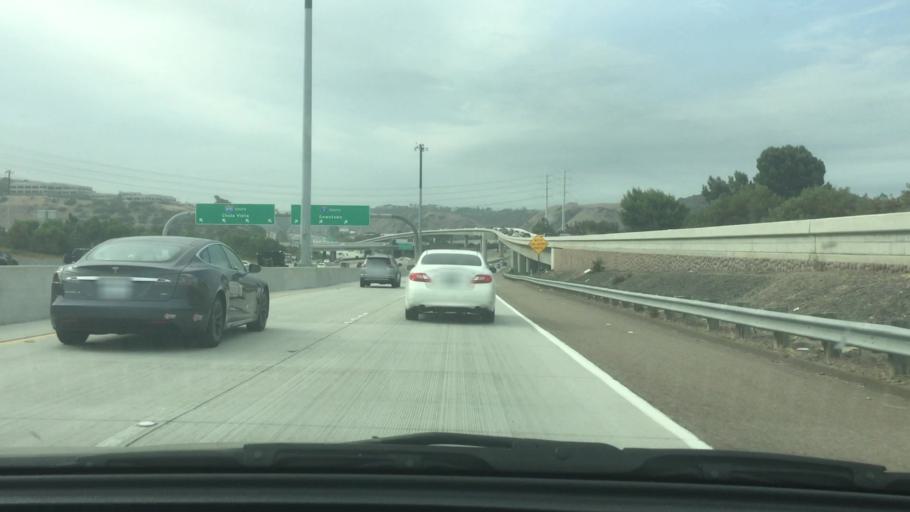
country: US
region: California
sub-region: San Diego County
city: Del Mar
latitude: 32.9085
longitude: -117.2272
